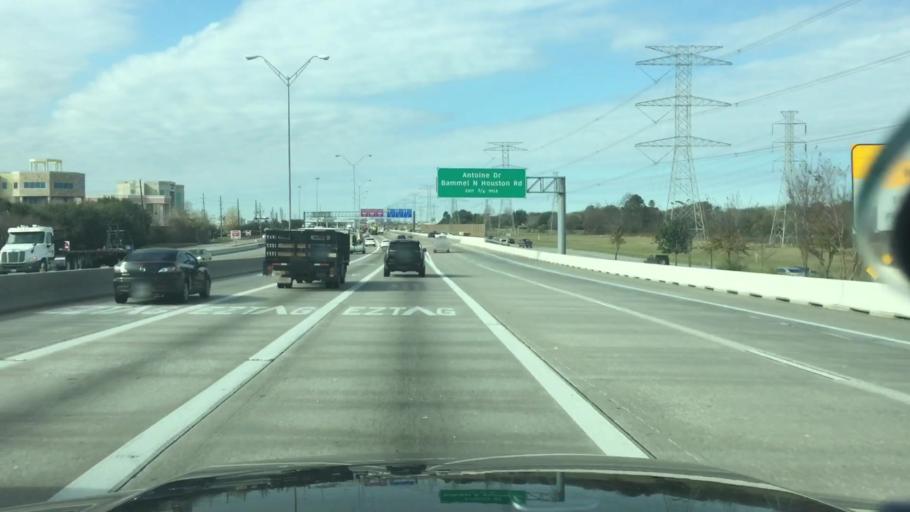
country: US
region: Texas
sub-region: Harris County
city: Hudson
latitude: 29.9377
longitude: -95.4631
